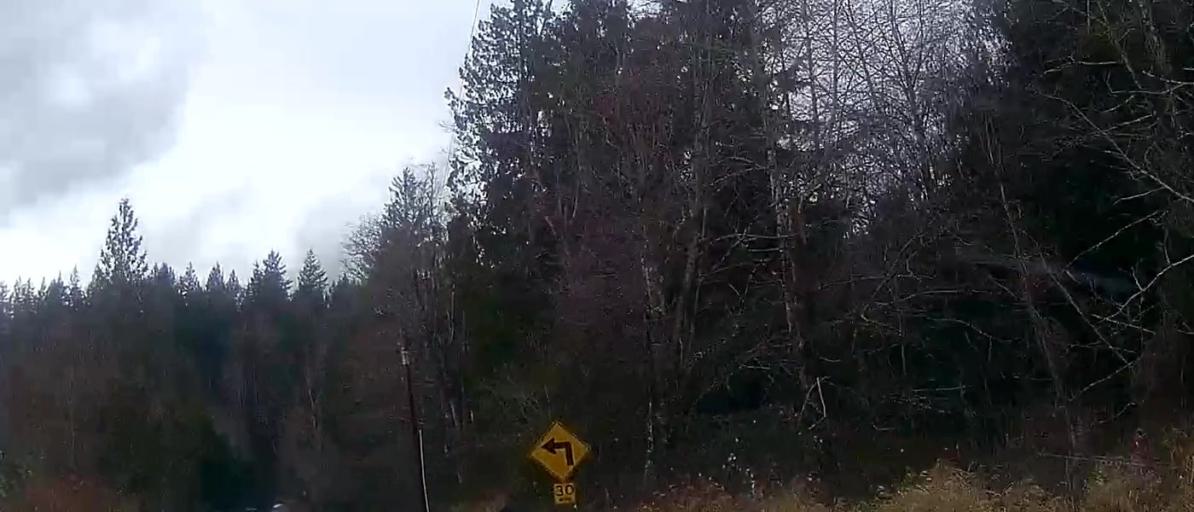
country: US
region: Washington
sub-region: Skagit County
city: Sedro-Woolley
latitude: 48.5870
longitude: -122.2404
